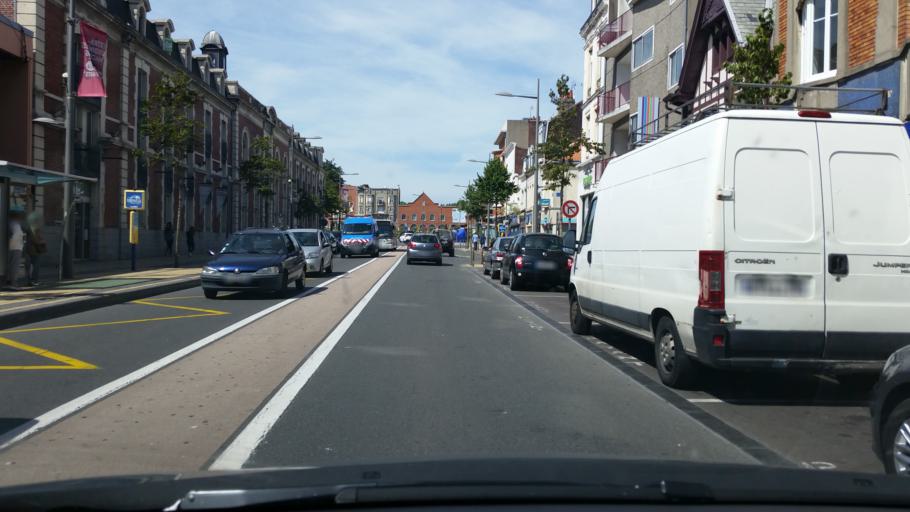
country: FR
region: Nord-Pas-de-Calais
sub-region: Departement du Pas-de-Calais
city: Calais
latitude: 50.9508
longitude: 1.8540
